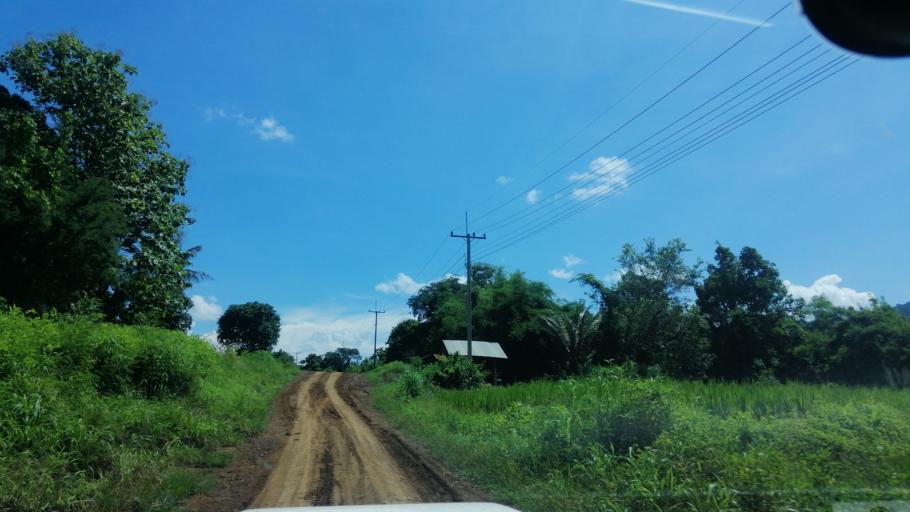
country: TH
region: Uttaradit
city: Ban Khok
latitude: 18.0894
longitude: 101.2429
